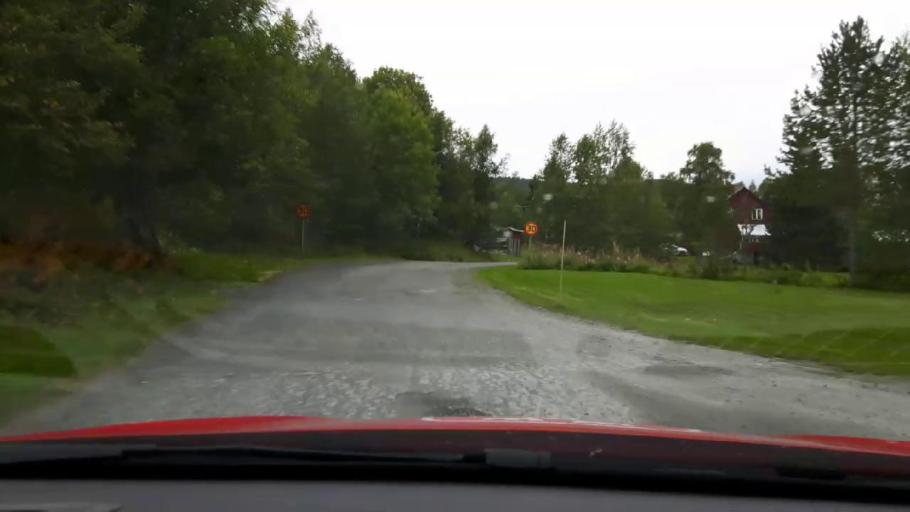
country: SE
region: Jaemtland
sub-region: Are Kommun
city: Are
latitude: 63.4891
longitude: 13.1273
